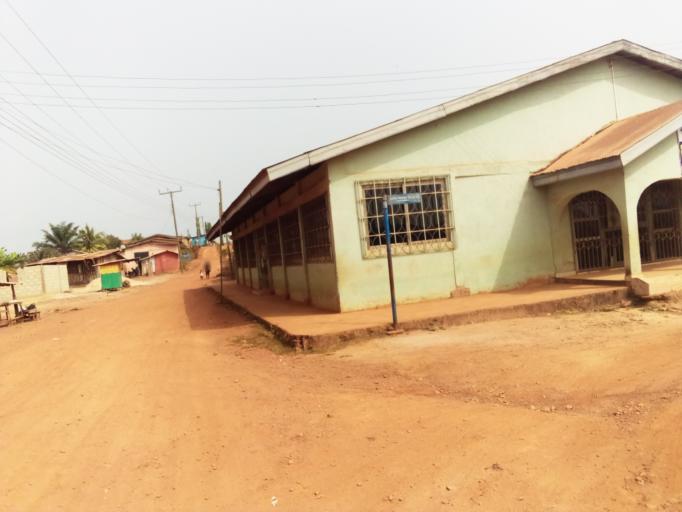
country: CI
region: Sud-Comoe
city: Ayame
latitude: 5.8284
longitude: -2.8196
